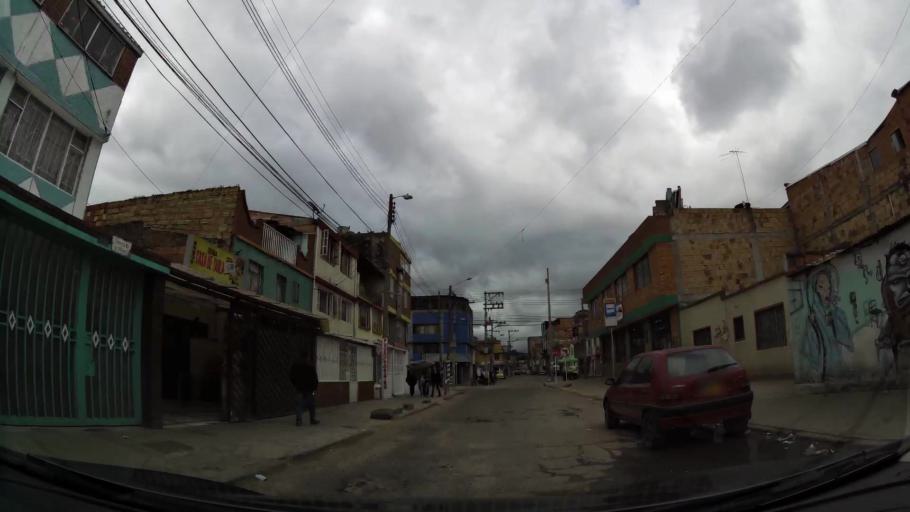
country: CO
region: Bogota D.C.
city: Barrio San Luis
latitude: 4.6973
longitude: -74.0995
